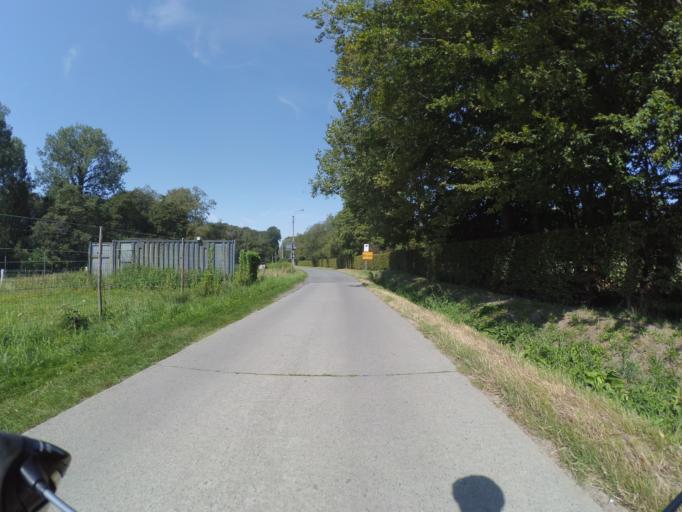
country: BE
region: Flanders
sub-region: Provincie West-Vlaanderen
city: Waregem
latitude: 50.8746
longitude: 3.4644
